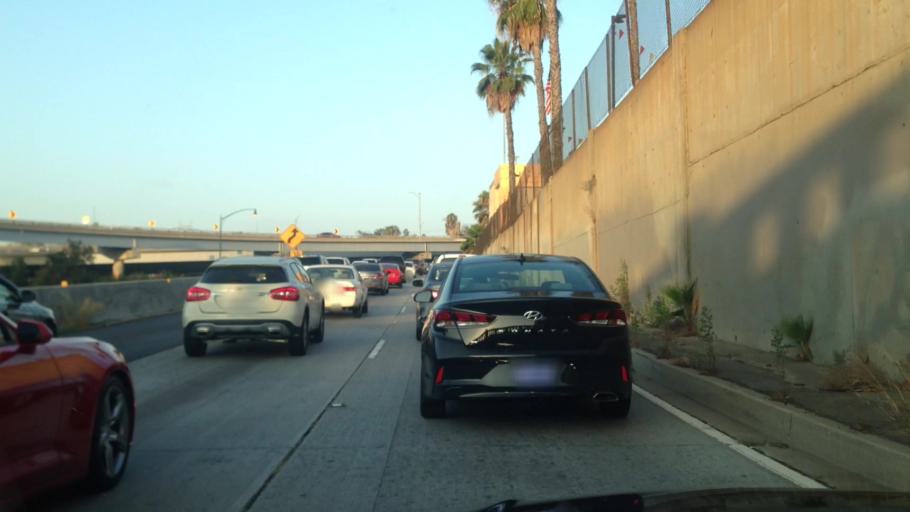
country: US
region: California
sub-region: Los Angeles County
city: Los Angeles
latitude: 34.0832
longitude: -118.2222
